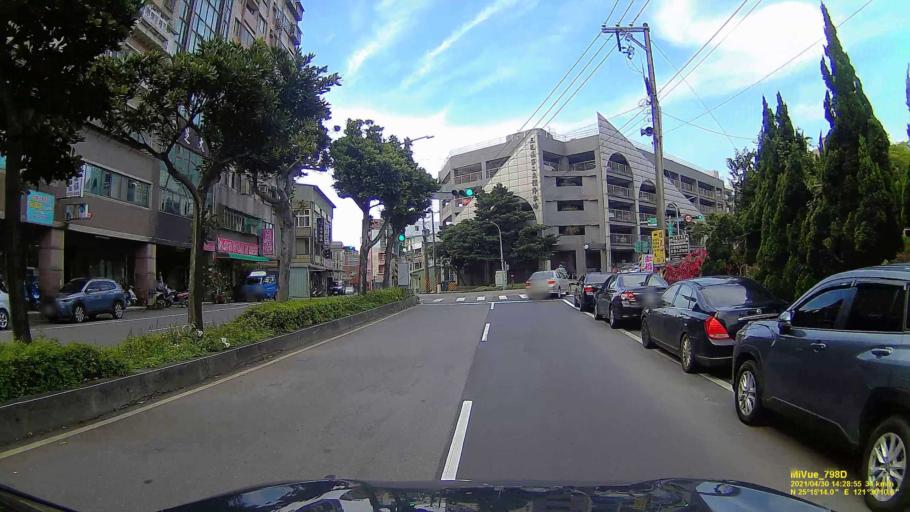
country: TW
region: Taipei
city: Taipei
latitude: 25.2537
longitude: 121.5029
